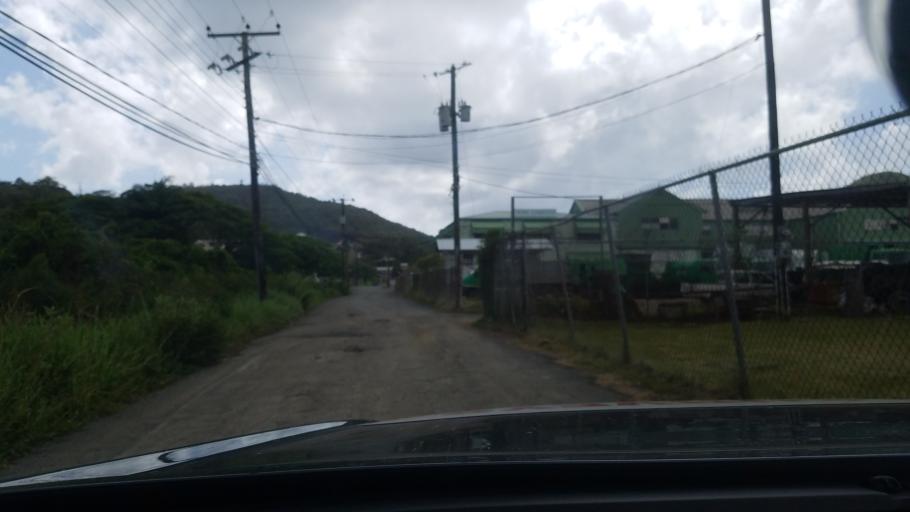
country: LC
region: Gros-Islet
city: Gros Islet
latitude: 14.0598
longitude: -60.9601
